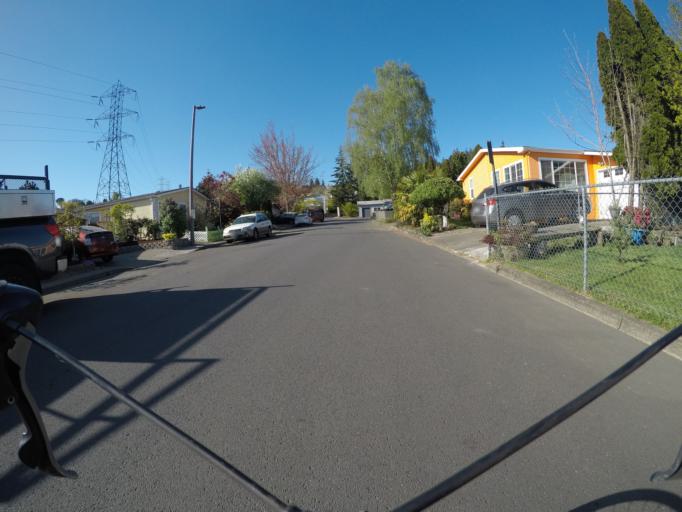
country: US
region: Oregon
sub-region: Washington County
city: King City
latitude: 45.4028
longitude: -122.8174
